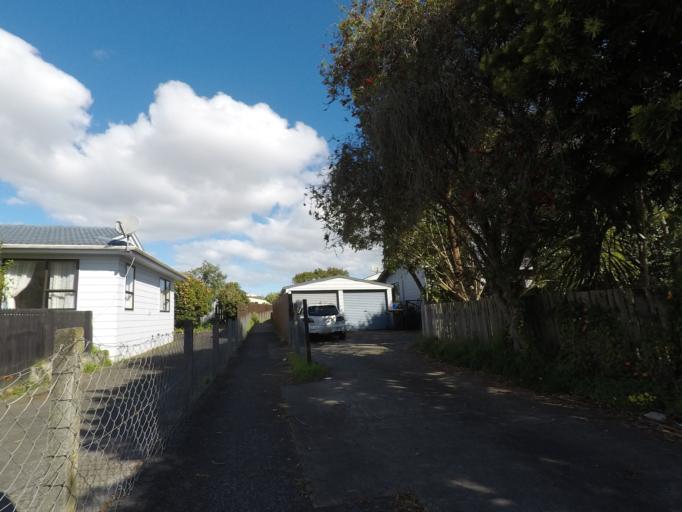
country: NZ
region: Auckland
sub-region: Auckland
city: Rosebank
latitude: -36.8597
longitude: 174.6017
